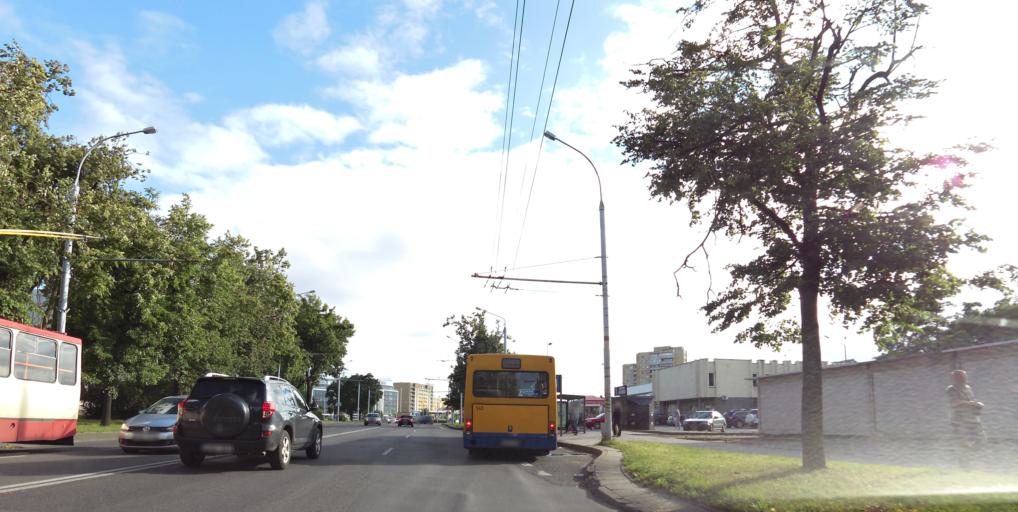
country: LT
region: Vilnius County
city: Rasos
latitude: 54.6978
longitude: 25.3007
